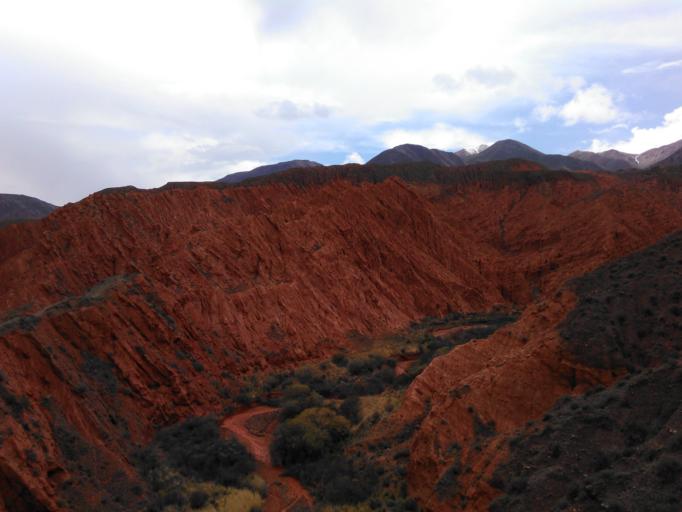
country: KG
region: Chuy
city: Bystrovka
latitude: 42.5755
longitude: 75.7044
